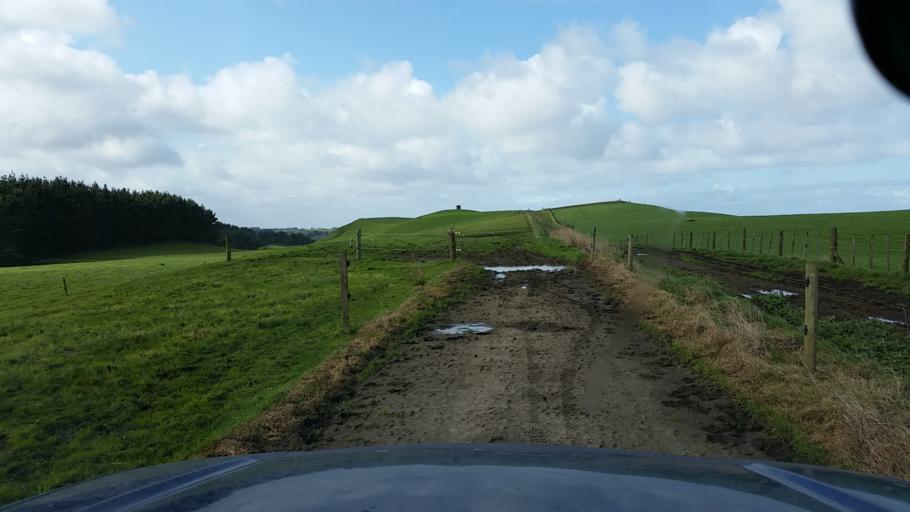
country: NZ
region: Taranaki
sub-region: South Taranaki District
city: Patea
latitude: -39.7448
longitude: 174.5361
